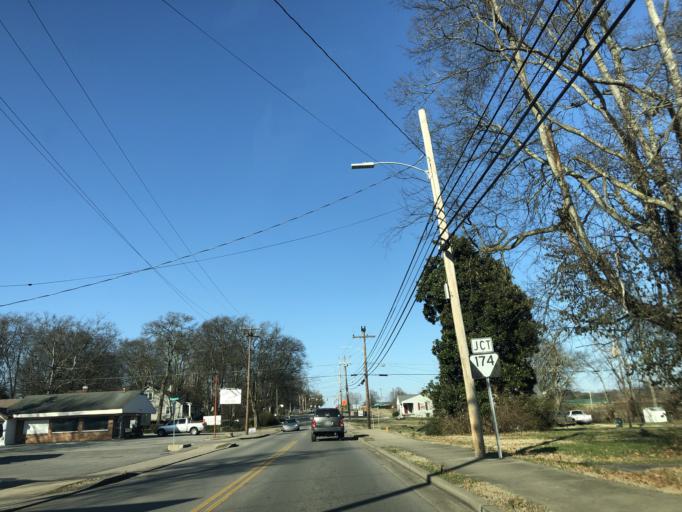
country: US
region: Tennessee
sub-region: Sumner County
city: Gallatin
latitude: 36.4019
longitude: -86.4455
